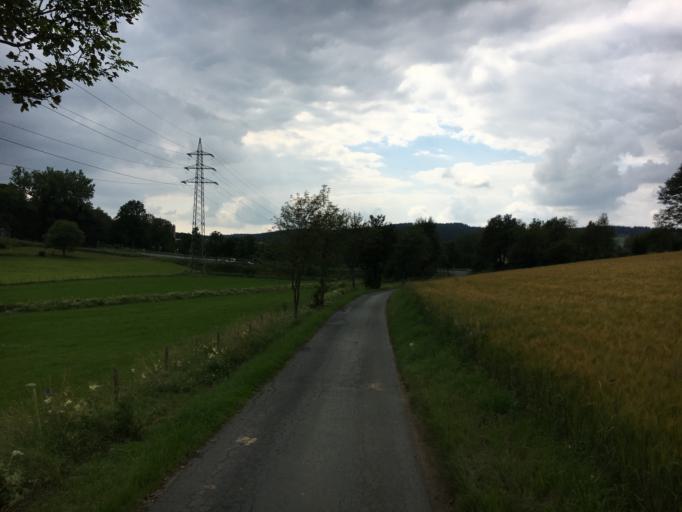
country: DE
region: North Rhine-Westphalia
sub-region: Regierungsbezirk Arnsberg
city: Erndtebruck
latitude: 50.9992
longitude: 8.2691
